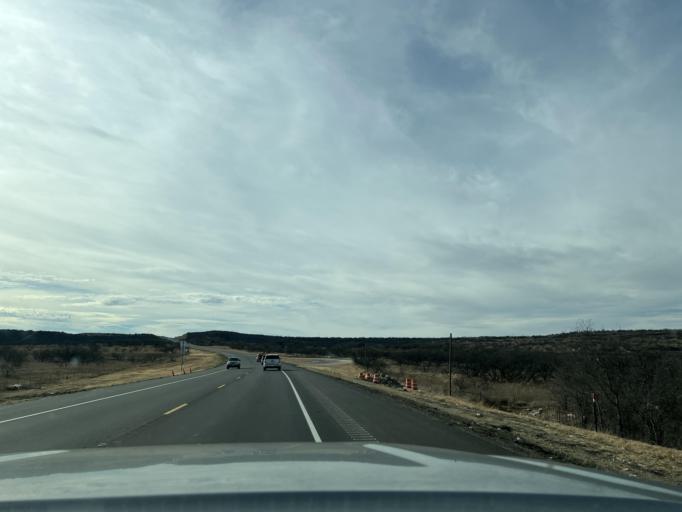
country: US
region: Texas
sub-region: Shackelford County
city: Albany
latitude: 32.7124
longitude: -99.3583
